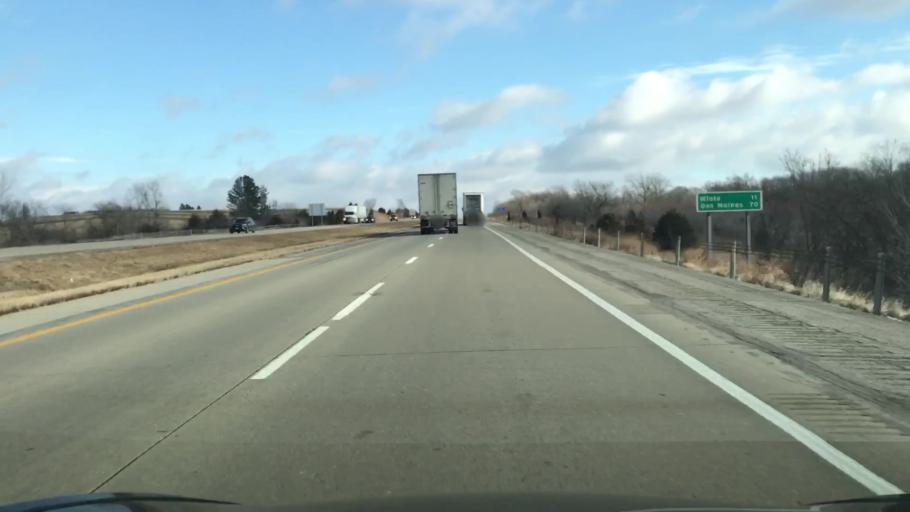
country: US
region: Iowa
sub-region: Cass County
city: Atlantic
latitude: 41.4970
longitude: -94.9266
